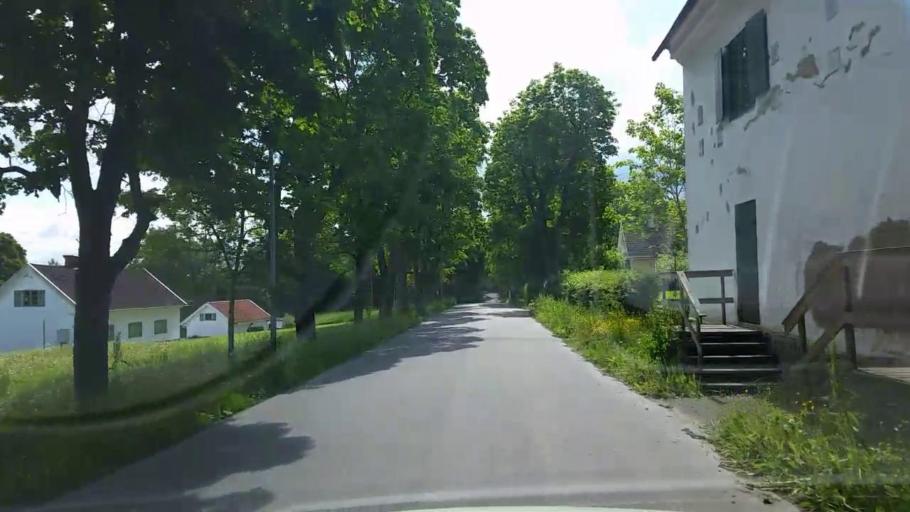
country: SE
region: Vaestmanland
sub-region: Fagersta Kommun
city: Fagersta
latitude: 60.0036
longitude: 15.7788
